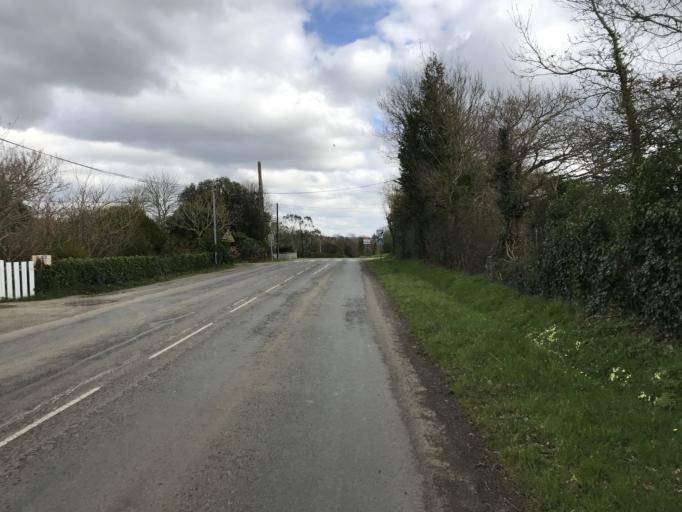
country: FR
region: Brittany
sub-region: Departement du Finistere
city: Hopital-Camfrout
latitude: 48.3255
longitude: -4.2305
